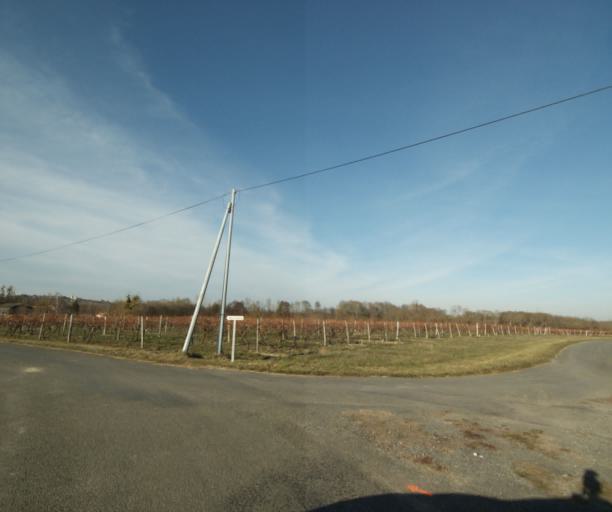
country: FR
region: Poitou-Charentes
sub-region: Departement de la Charente-Maritime
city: Burie
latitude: 45.7858
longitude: -0.4174
